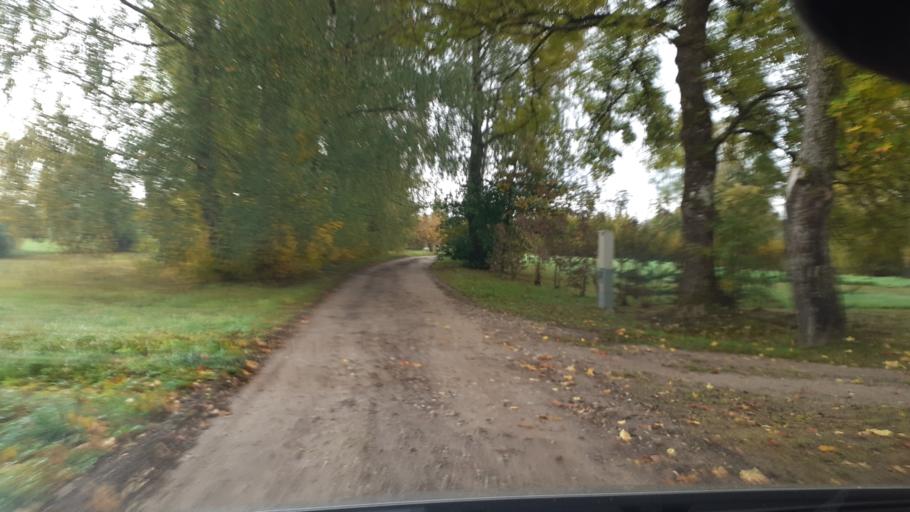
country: LV
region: Kuldigas Rajons
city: Kuldiga
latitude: 56.9730
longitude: 21.9393
